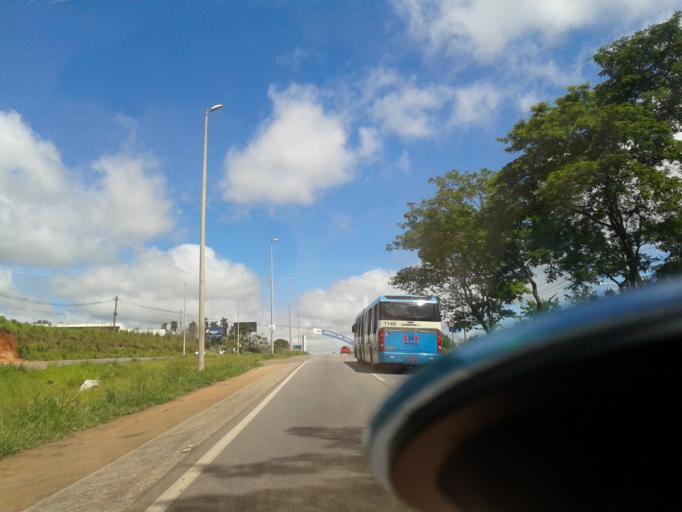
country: BR
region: Goias
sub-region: Goiania
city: Goiania
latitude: -16.6412
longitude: -49.3412
